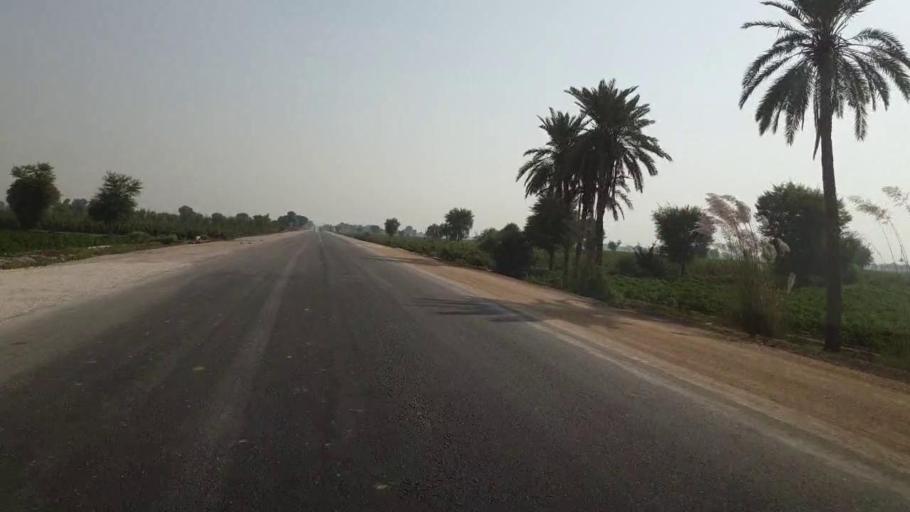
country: PK
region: Sindh
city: Bhan
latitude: 26.5454
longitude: 67.7870
